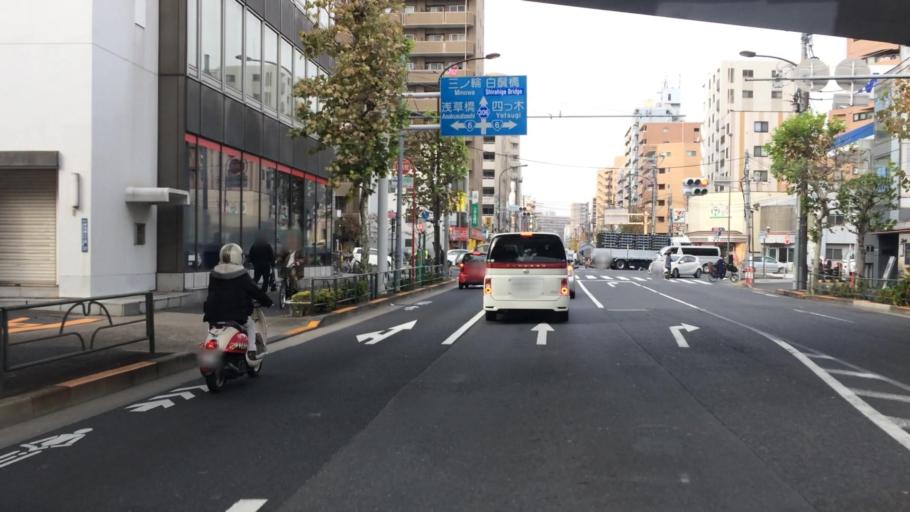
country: JP
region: Tokyo
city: Urayasu
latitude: 35.7220
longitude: 139.8188
